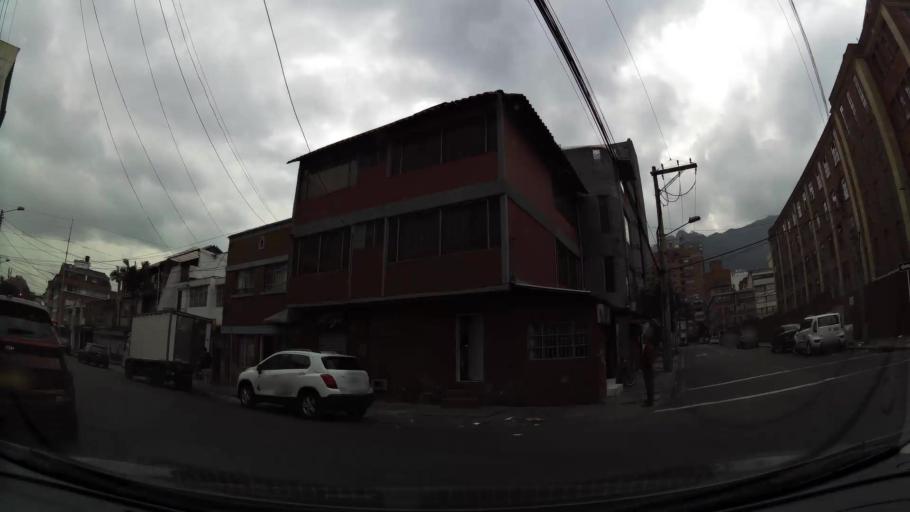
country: CO
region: Bogota D.C.
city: Barrio San Luis
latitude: 4.6516
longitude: -74.0610
